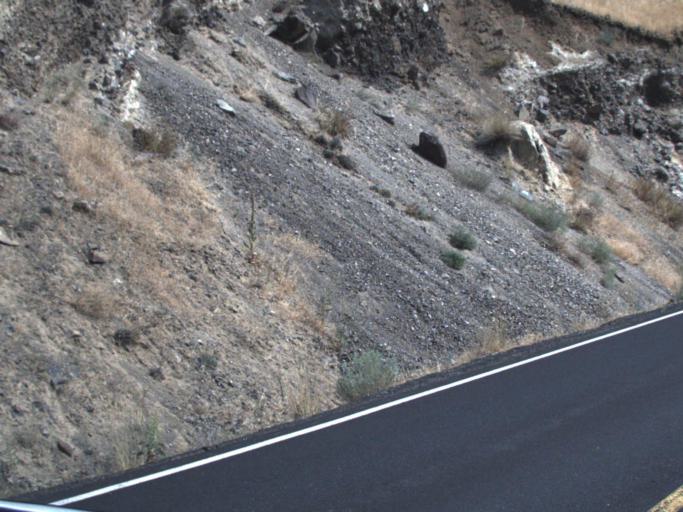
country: US
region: Washington
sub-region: Yakima County
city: Selah
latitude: 46.7283
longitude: -120.4515
